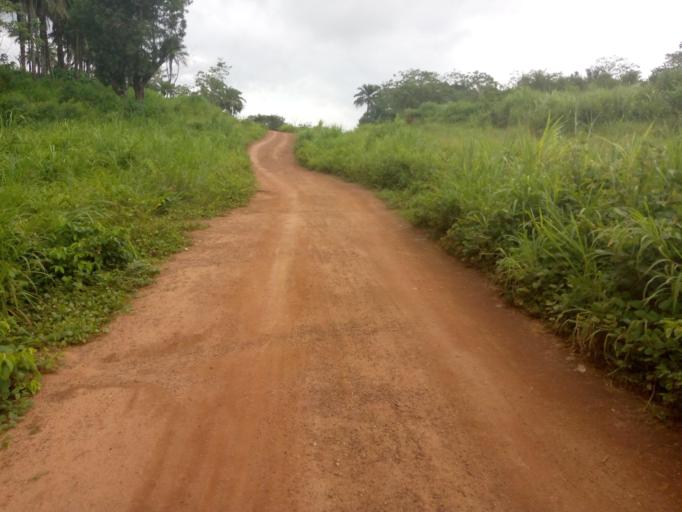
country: SL
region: Eastern Province
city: Buedu
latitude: 8.4717
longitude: -10.3339
